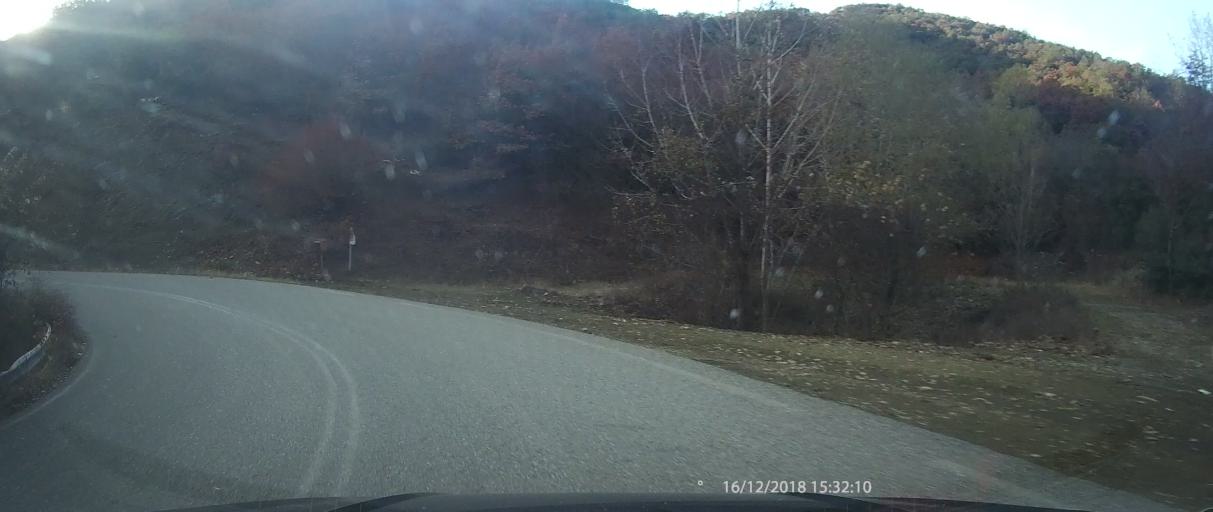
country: GR
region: Epirus
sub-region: Nomos Ioanninon
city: Konitsa
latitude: 40.0721
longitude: 20.7401
